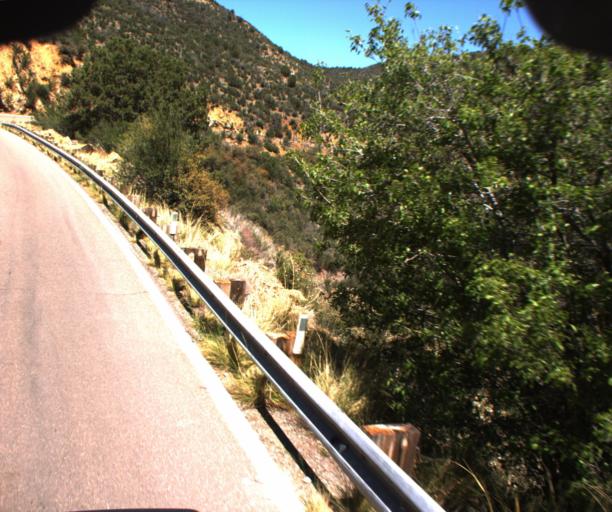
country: US
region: Arizona
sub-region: Yavapai County
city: Prescott
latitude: 34.4652
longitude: -112.5199
